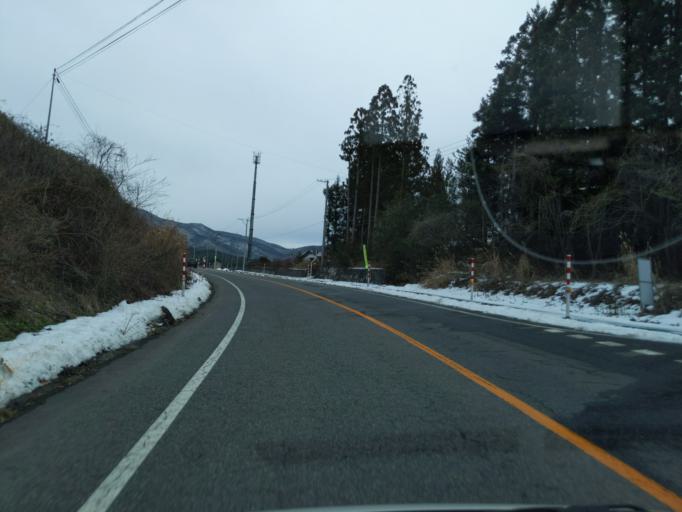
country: JP
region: Iwate
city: Mizusawa
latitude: 39.1173
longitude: 141.2585
